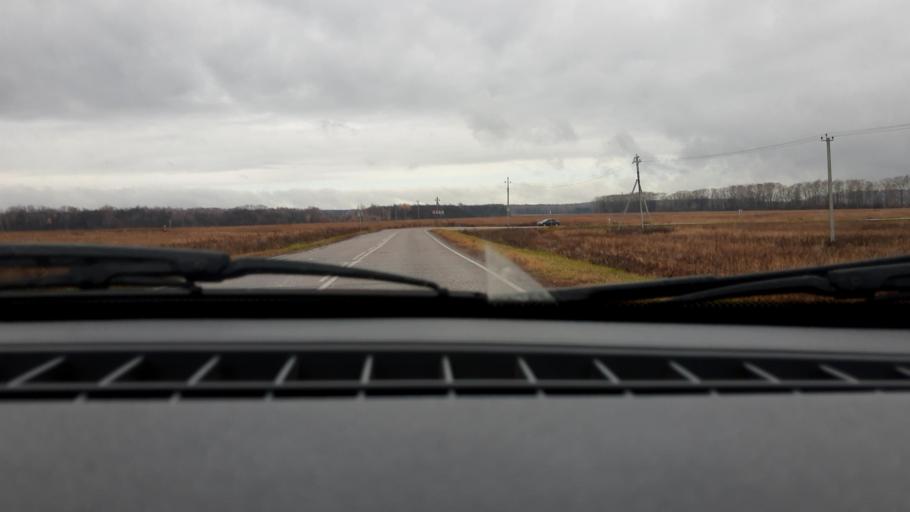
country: RU
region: Bashkortostan
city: Mikhaylovka
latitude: 54.8178
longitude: 55.7699
